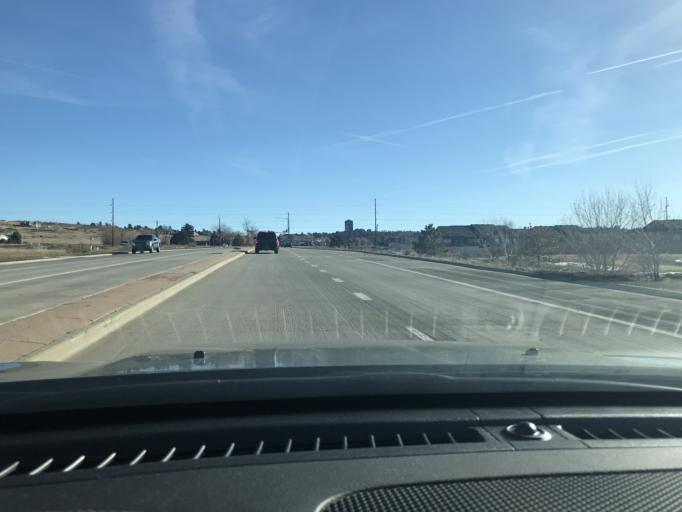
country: US
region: Colorado
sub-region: Douglas County
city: Parker
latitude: 39.5363
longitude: -104.7585
